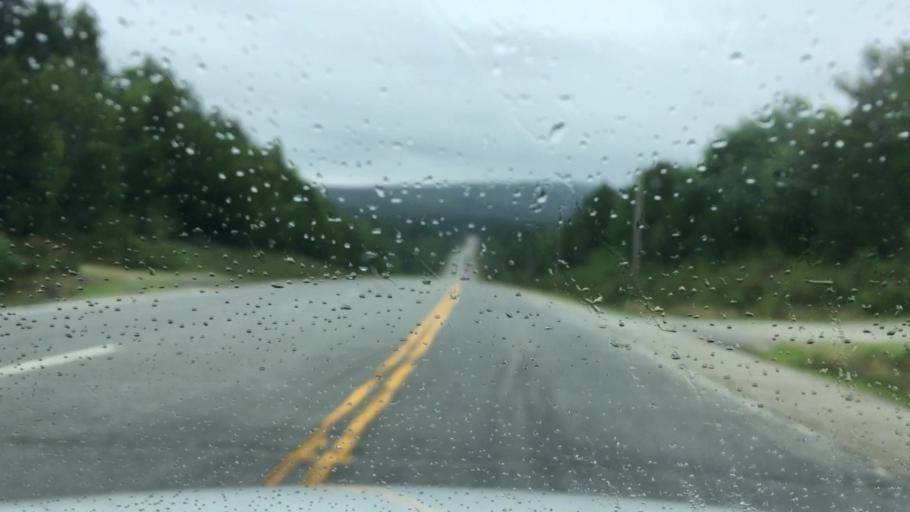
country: US
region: Maine
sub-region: Hancock County
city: Franklin
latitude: 44.8251
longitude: -68.1027
